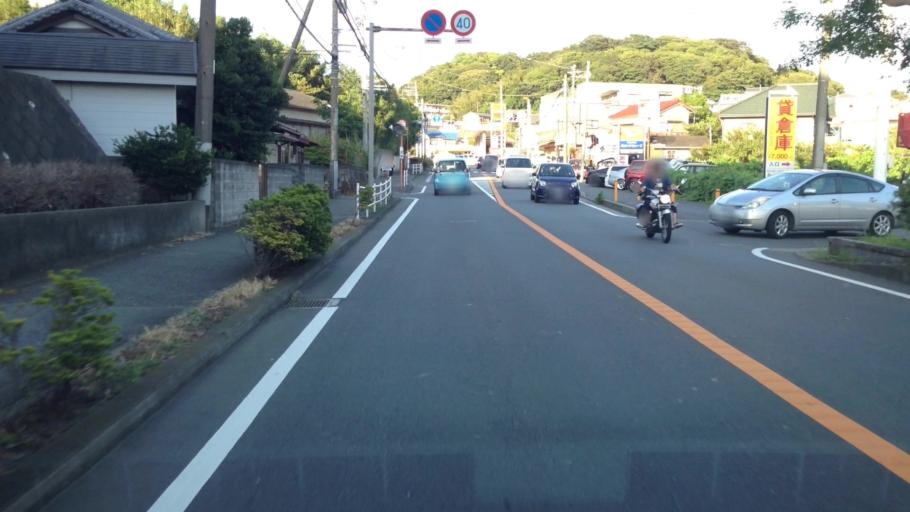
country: JP
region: Kanagawa
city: Yokosuka
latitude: 35.2264
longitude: 139.6486
